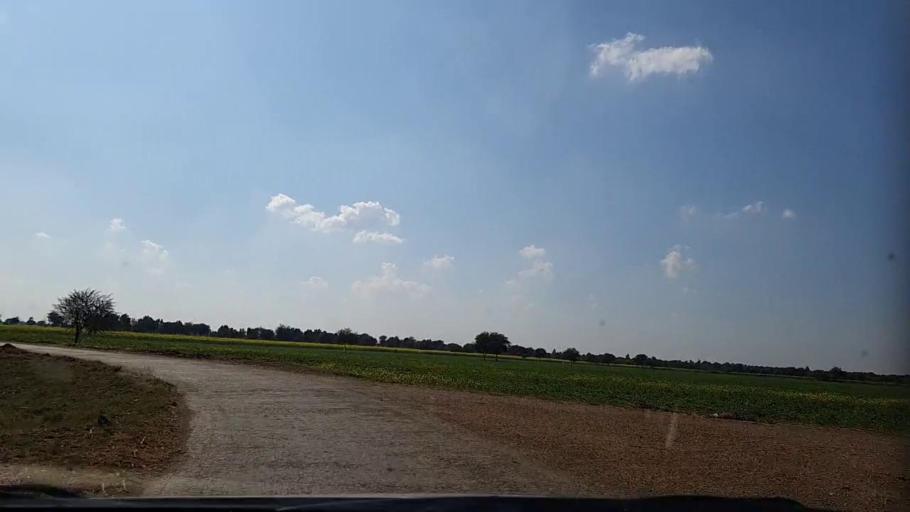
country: PK
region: Sindh
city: Pithoro
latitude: 25.6689
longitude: 69.4620
